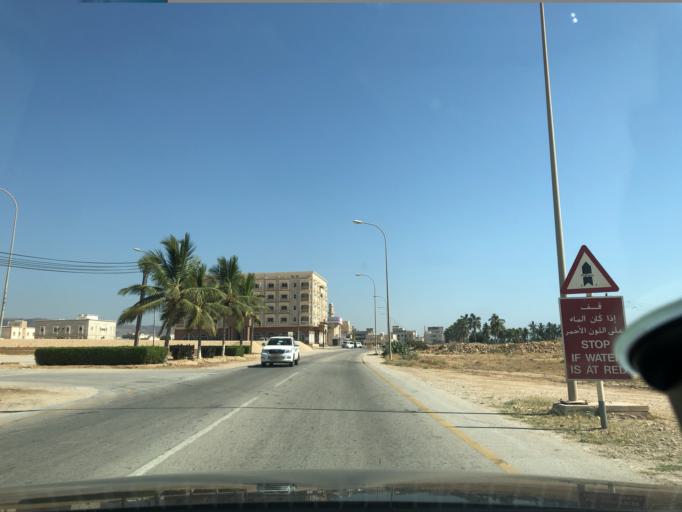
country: OM
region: Zufar
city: Salalah
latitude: 17.0394
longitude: 54.3847
